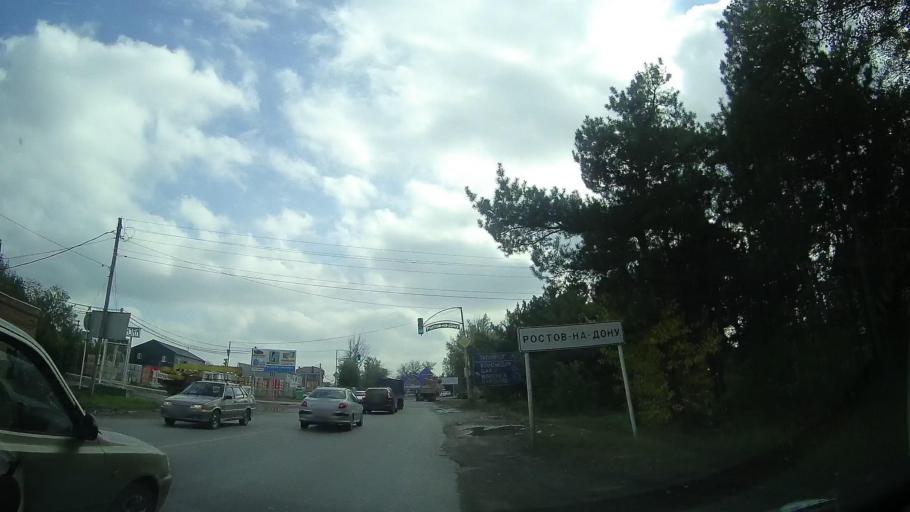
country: RU
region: Rostov
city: Severnyy
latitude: 47.2937
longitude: 39.6600
